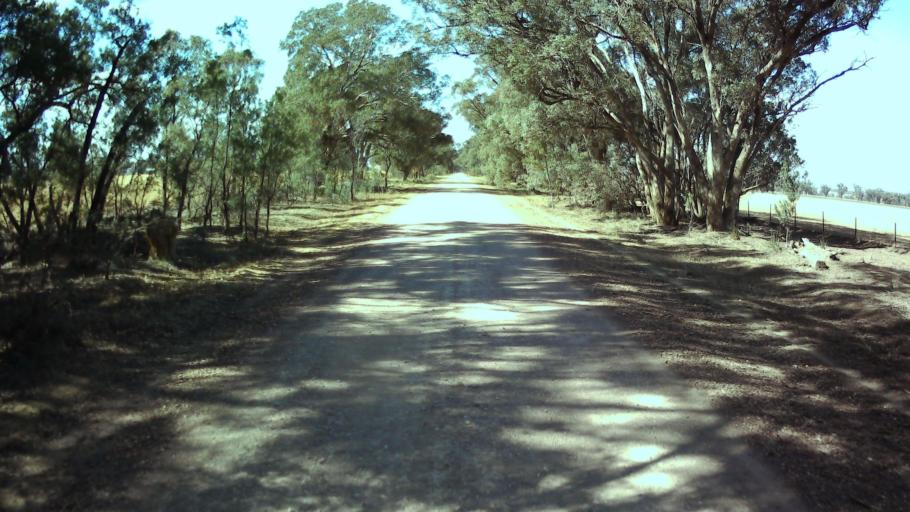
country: AU
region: New South Wales
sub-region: Weddin
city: Grenfell
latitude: -34.0373
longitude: 148.3164
